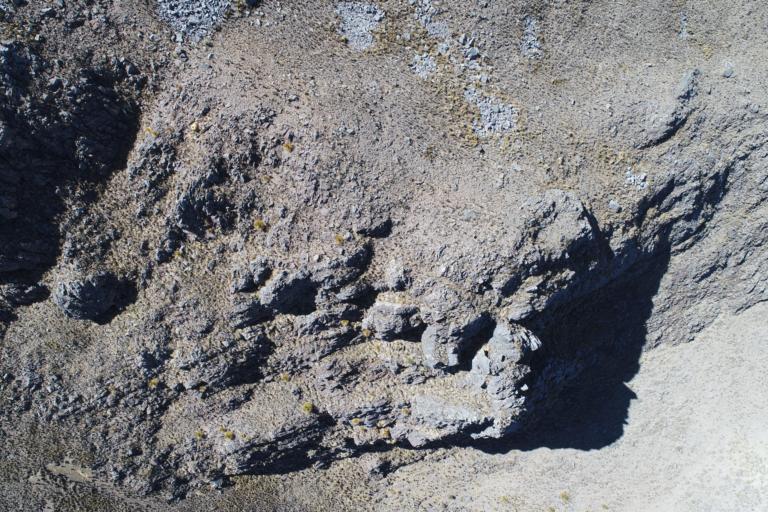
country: BO
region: La Paz
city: Viloco
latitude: -16.8053
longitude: -67.5450
